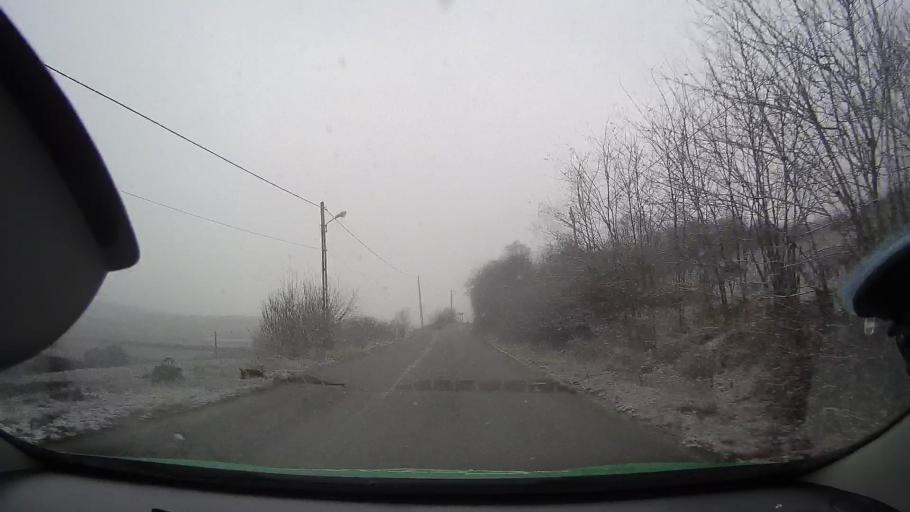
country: RO
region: Alba
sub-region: Comuna Noslac
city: Noslac
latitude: 46.3561
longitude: 23.9317
